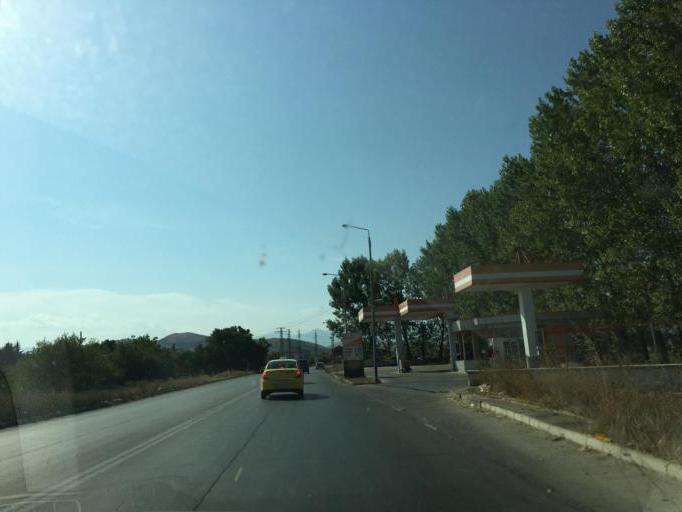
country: BG
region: Pazardzhik
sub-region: Obshtina Pazardzhik
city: Pazardzhik
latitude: 42.1663
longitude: 24.3153
